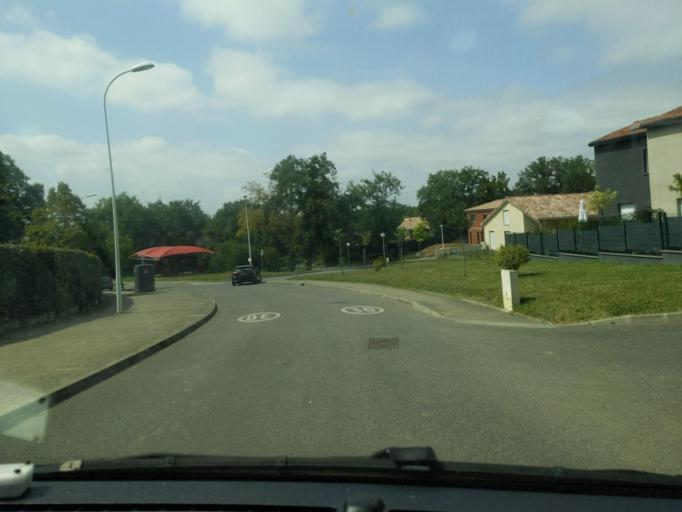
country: FR
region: Midi-Pyrenees
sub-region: Departement de la Haute-Garonne
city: Balma
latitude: 43.6115
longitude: 1.5191
